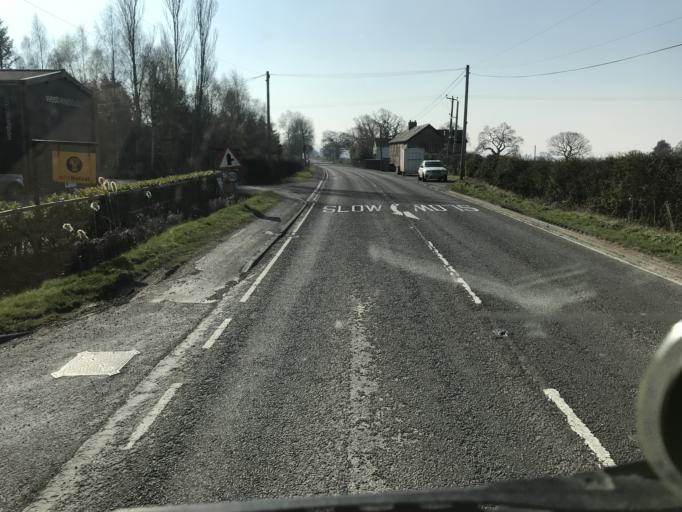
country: GB
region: England
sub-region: Cheshire West and Chester
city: Waverton
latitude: 53.1420
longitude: -2.8117
